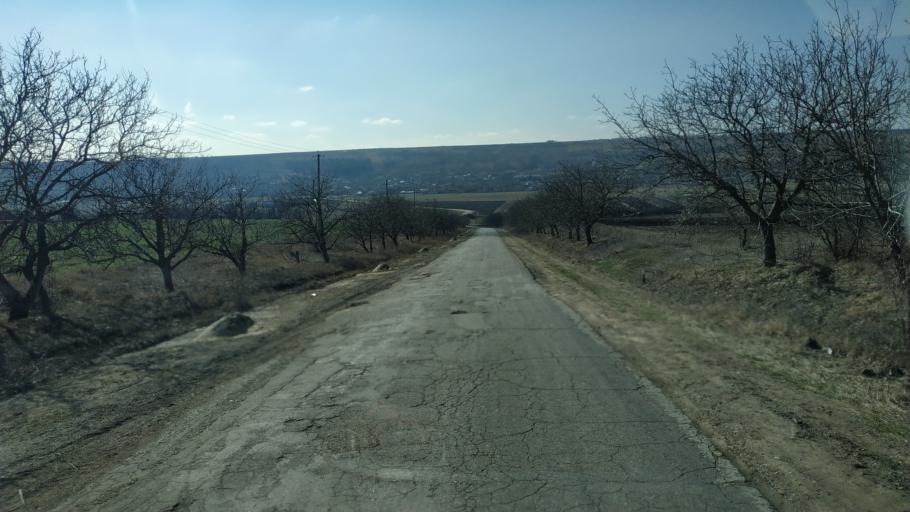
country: MD
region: Hincesti
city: Hincesti
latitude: 46.7580
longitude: 28.6601
